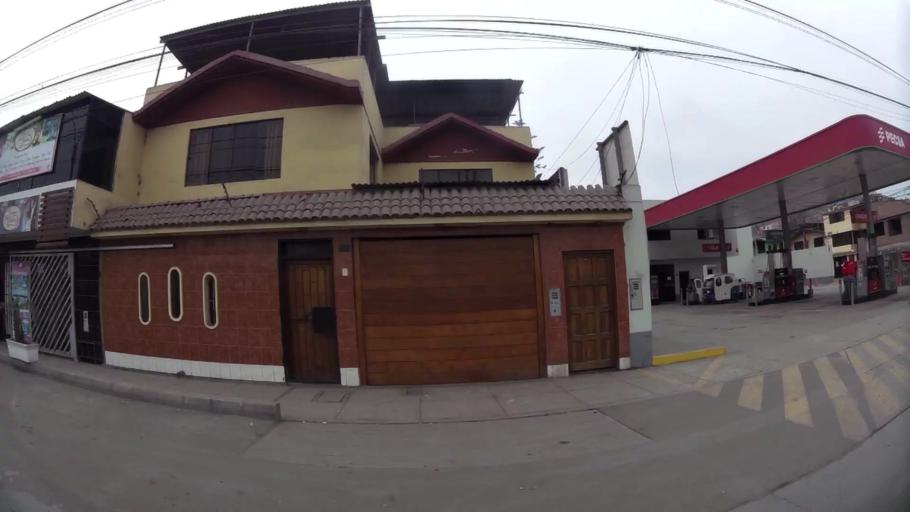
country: PE
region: Lima
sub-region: Lima
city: Cieneguilla
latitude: -12.2241
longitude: -76.9084
